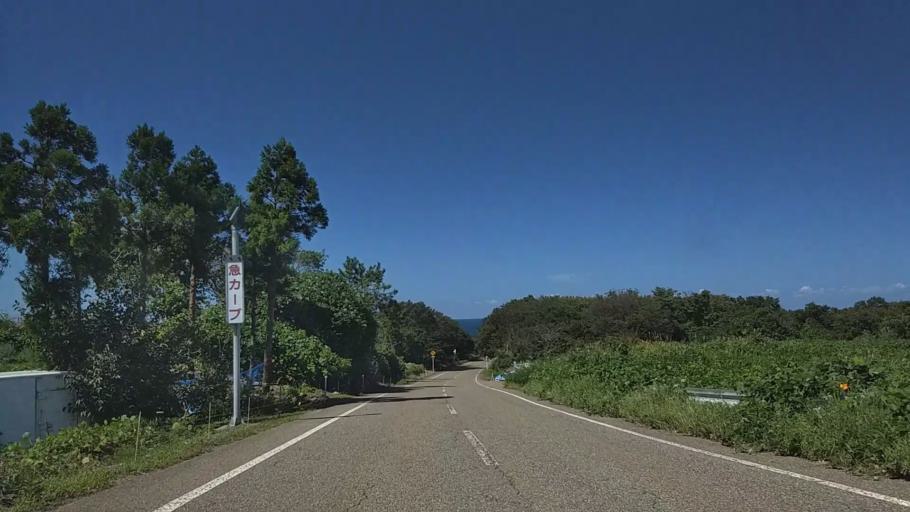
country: JP
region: Niigata
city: Joetsu
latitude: 37.1707
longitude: 138.1053
